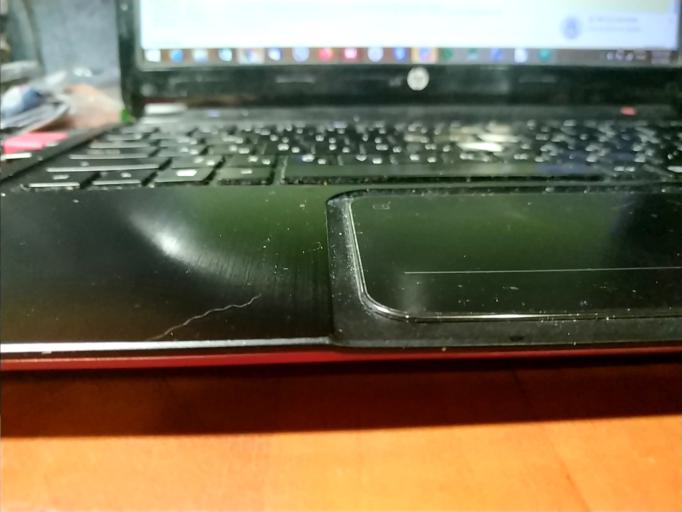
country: RU
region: Vologda
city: Suda
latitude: 58.9134
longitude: 37.5432
